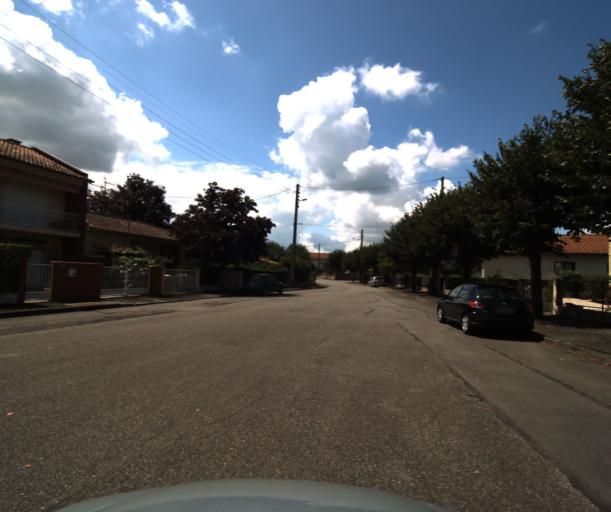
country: FR
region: Midi-Pyrenees
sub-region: Departement de la Haute-Garonne
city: Portet-sur-Garonne
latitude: 43.5195
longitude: 1.4017
